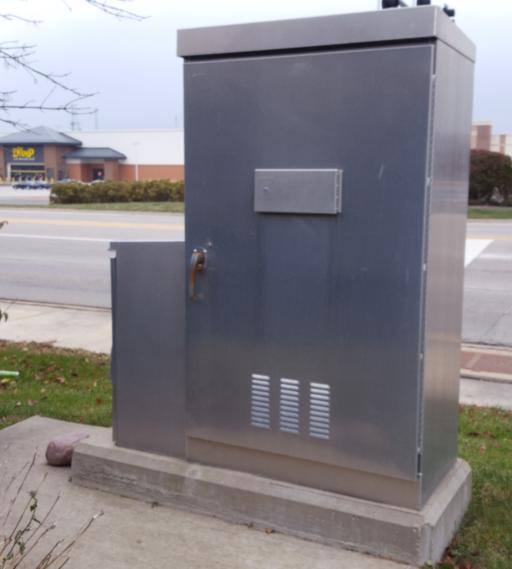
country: US
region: Illinois
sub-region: Cook County
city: Northbrook
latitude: 42.1496
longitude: -87.8331
